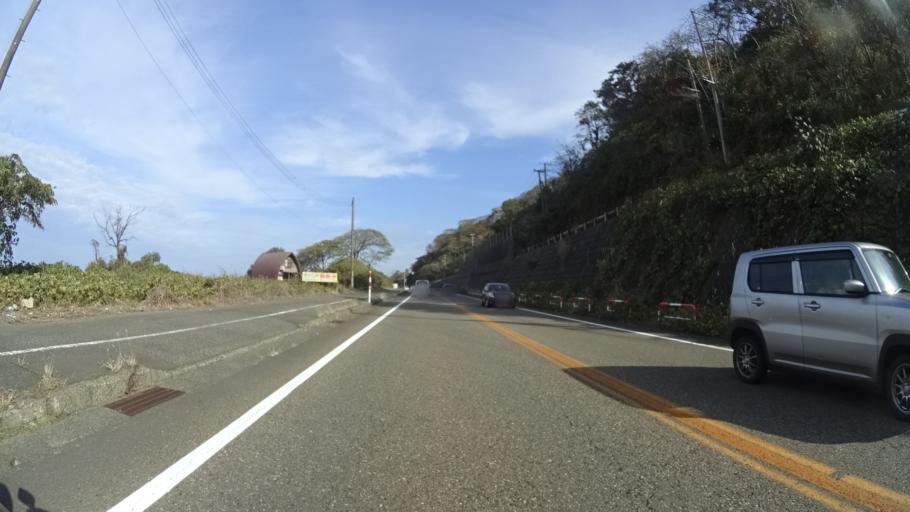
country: JP
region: Niigata
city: Joetsu
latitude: 37.1677
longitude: 138.1897
